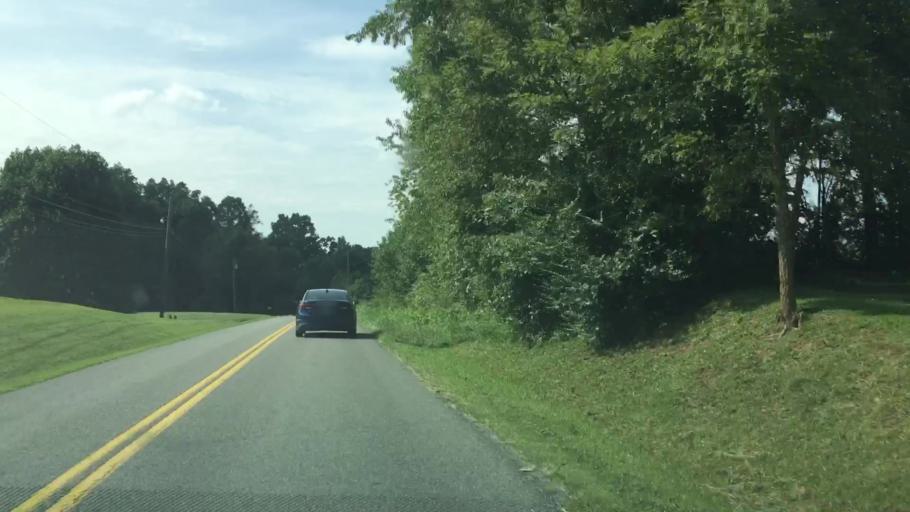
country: US
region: Tennessee
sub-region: Sullivan County
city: Fairmount
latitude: 36.5991
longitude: -82.0510
